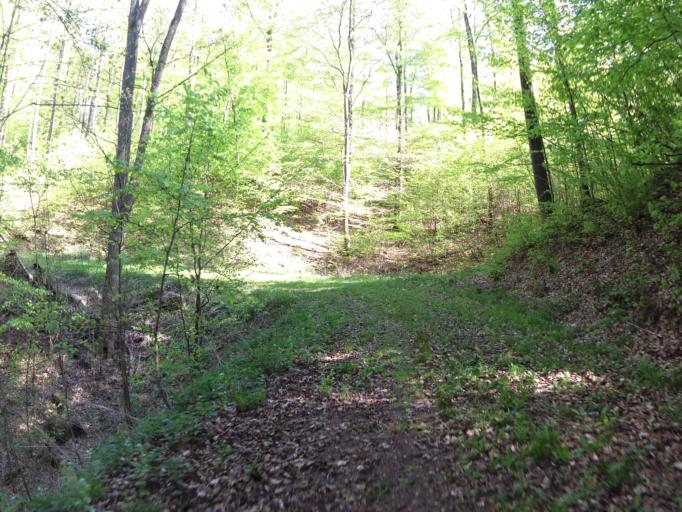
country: DE
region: Thuringia
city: Wolfsburg-Unkeroda
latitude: 50.9655
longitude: 10.2661
